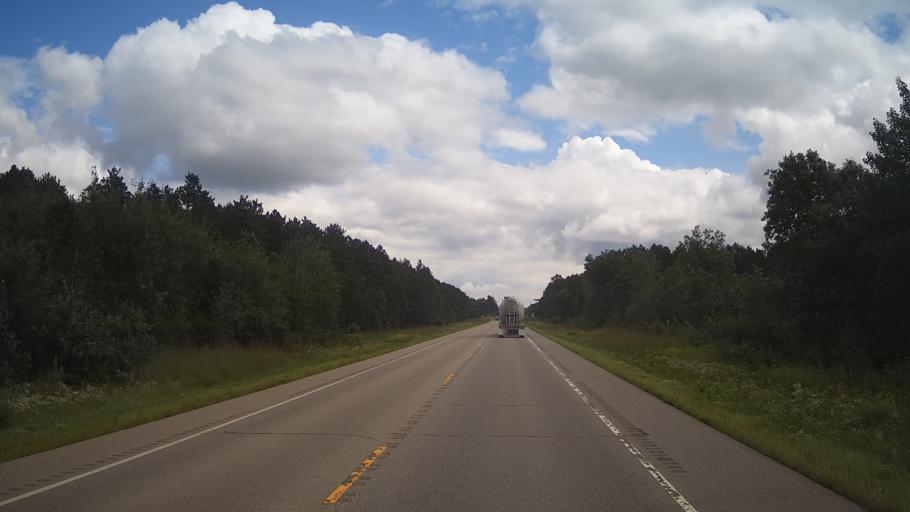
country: US
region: Wisconsin
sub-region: Marquette County
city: Westfield
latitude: 44.0220
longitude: -89.6245
